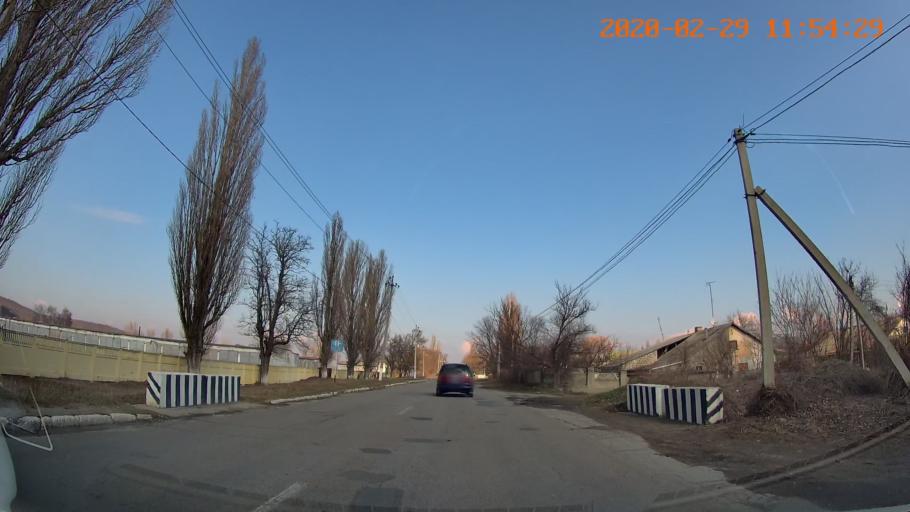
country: MD
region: Telenesti
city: Ribnita
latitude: 47.7846
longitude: 28.9952
